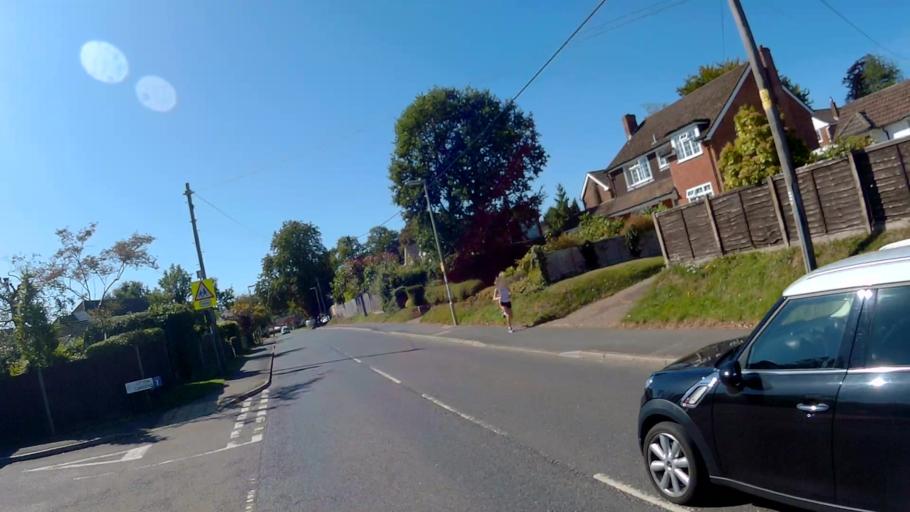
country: GB
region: England
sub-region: Hampshire
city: Overton
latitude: 51.2504
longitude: -1.1769
